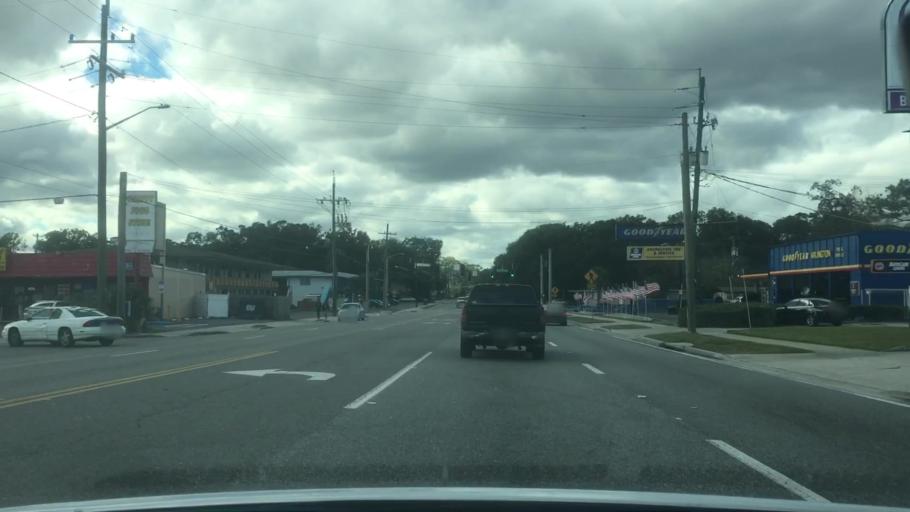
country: US
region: Florida
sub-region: Duval County
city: Jacksonville
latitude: 30.3518
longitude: -81.5978
